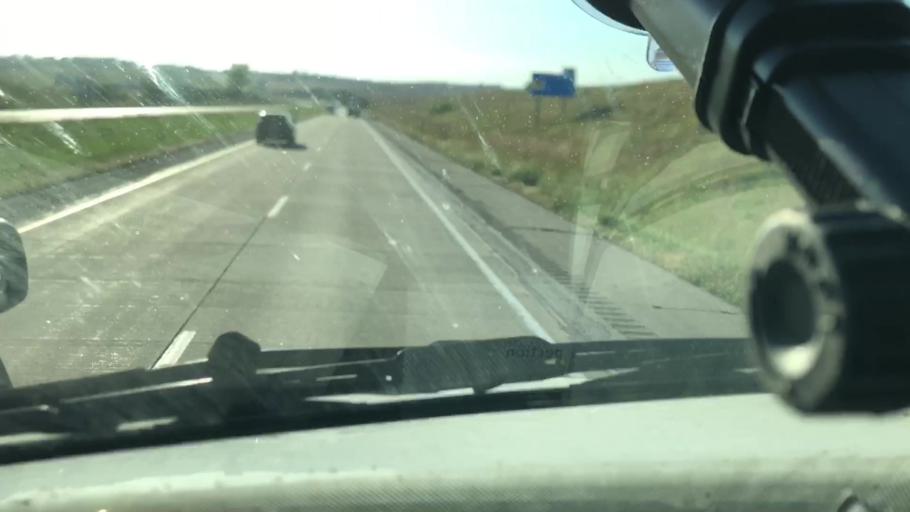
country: US
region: Iowa
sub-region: Pottawattamie County
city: Avoca
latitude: 41.5002
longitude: -95.5126
